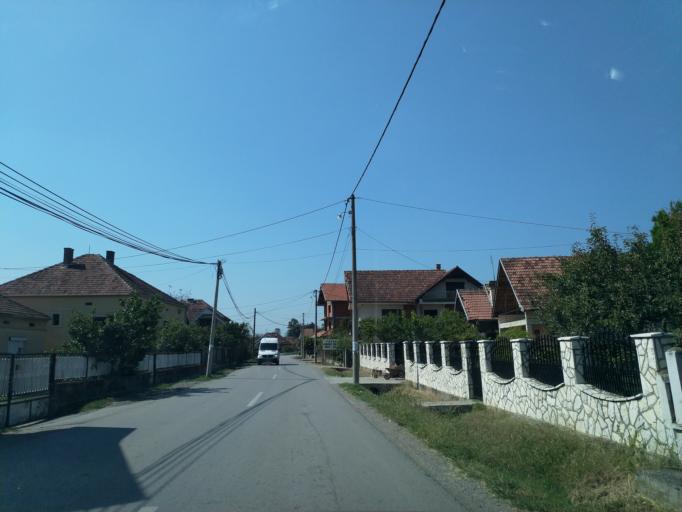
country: RS
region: Central Serbia
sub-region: Rasinski Okrug
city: Trstenik
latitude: 43.6258
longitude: 21.1358
